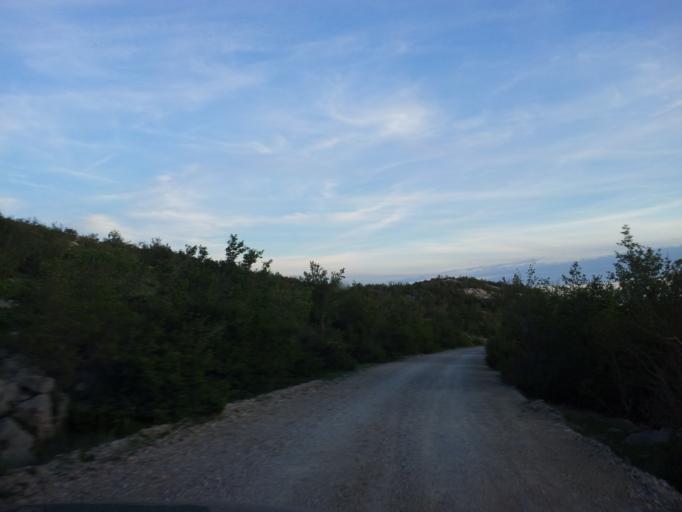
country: HR
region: Zadarska
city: Obrovac
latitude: 44.2579
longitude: 15.6344
